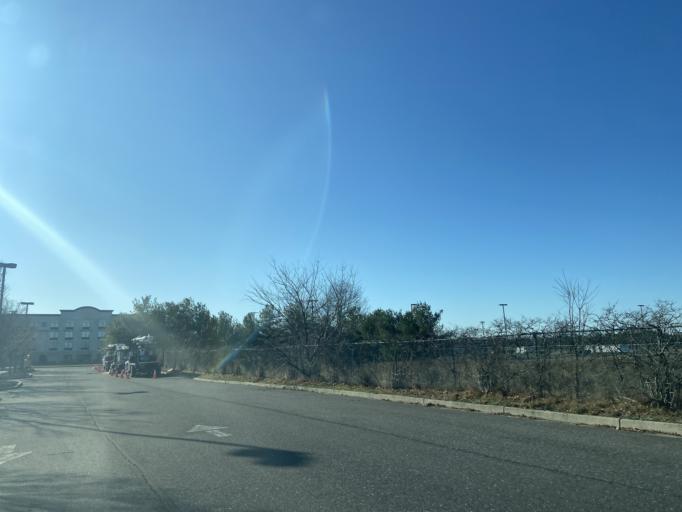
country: US
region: New Jersey
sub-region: Cumberland County
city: Vineland
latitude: 39.4907
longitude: -75.0666
